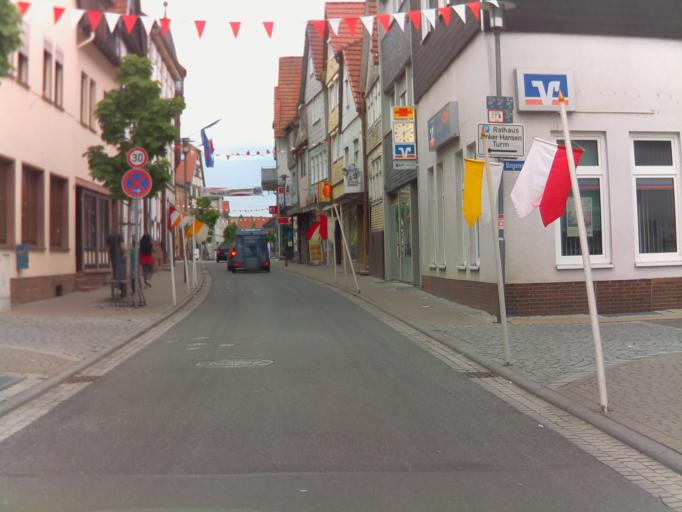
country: DE
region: Hesse
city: Neustadt (Hessen)
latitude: 50.8525
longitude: 9.1159
